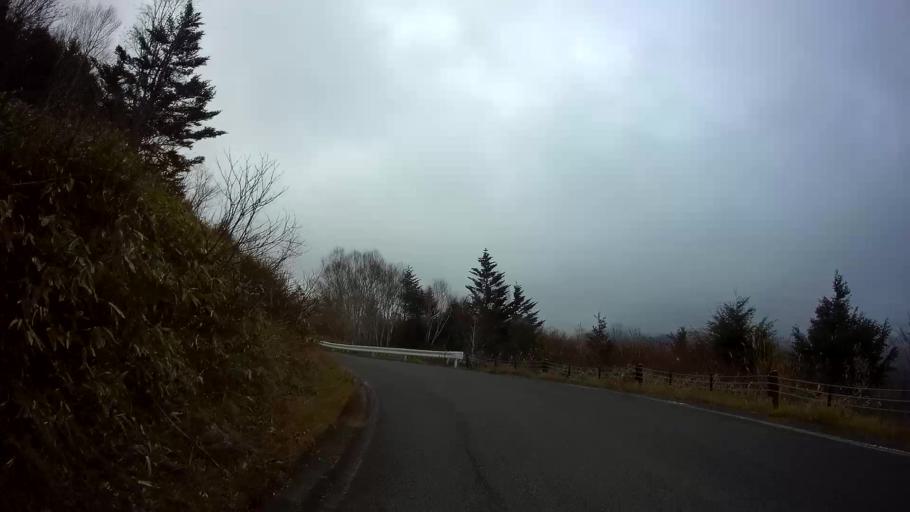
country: JP
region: Gunma
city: Nakanojomachi
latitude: 36.7175
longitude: 138.6472
